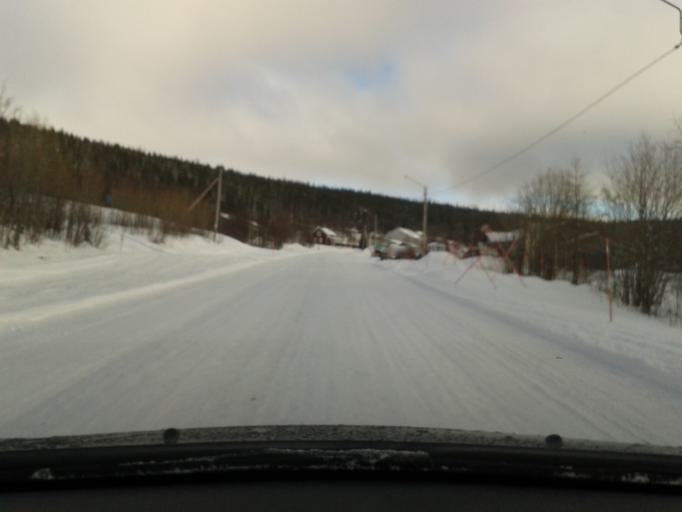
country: SE
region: Vaesterbotten
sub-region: Vilhelmina Kommun
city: Sjoberg
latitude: 65.2536
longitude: 15.5148
